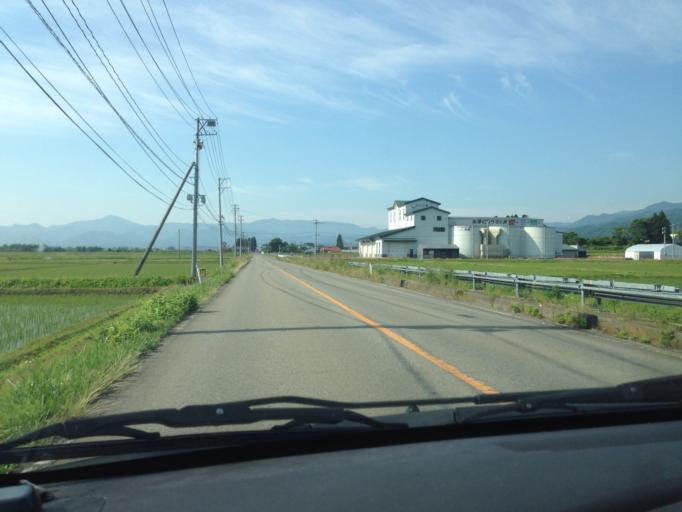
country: JP
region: Fukushima
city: Kitakata
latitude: 37.5152
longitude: 139.8344
